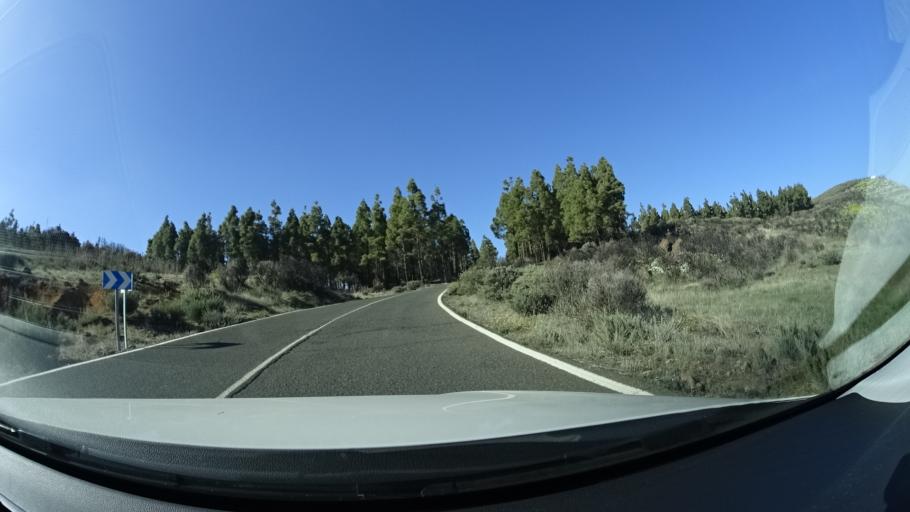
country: ES
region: Canary Islands
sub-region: Provincia de Las Palmas
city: San Bartolome
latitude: 27.9652
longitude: -15.5596
